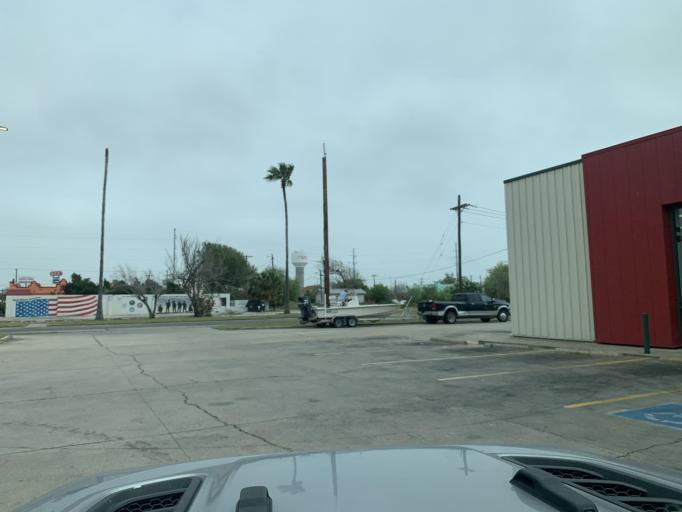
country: US
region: Texas
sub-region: San Patricio County
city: Aransas Pass
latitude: 27.8997
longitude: -97.1477
